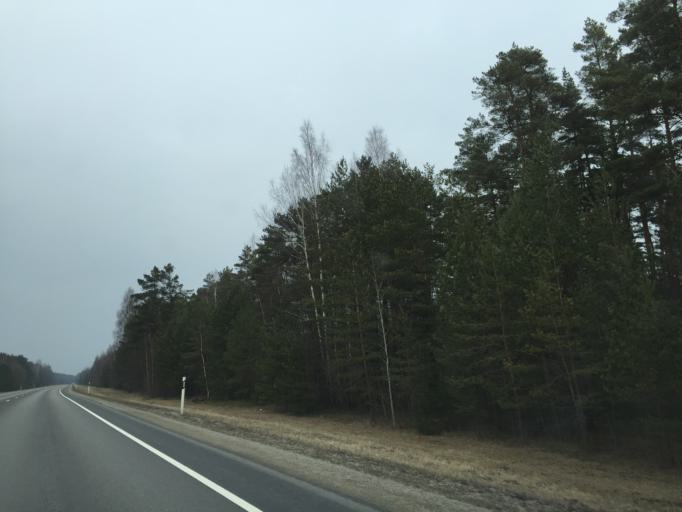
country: LV
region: Salacgrivas
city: Ainazi
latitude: 58.0913
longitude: 24.5078
